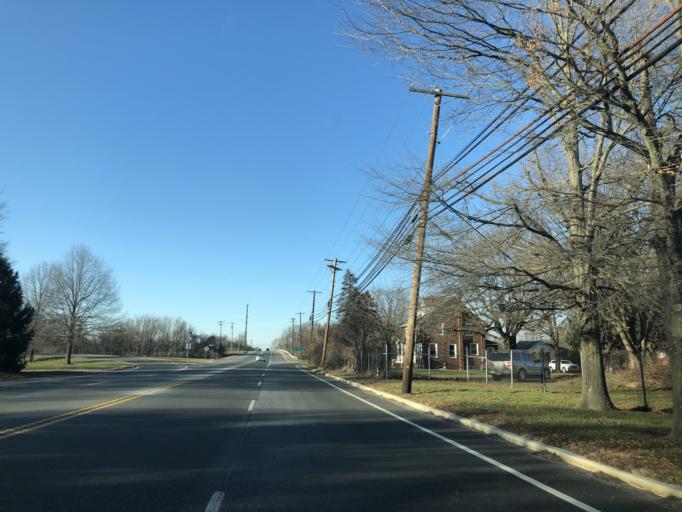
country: US
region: New Jersey
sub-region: Salem County
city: Carneys Point
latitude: 39.7060
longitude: -75.4437
